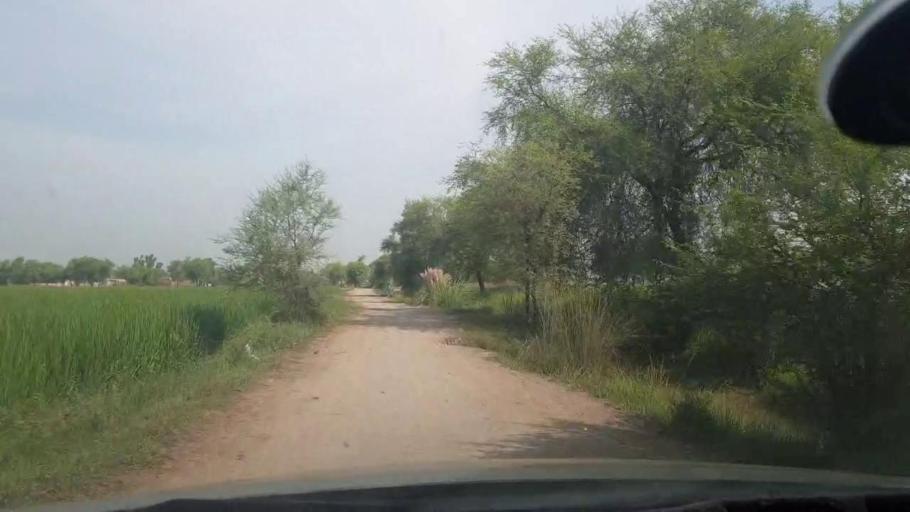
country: PK
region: Sindh
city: Jacobabad
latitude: 28.2943
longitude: 68.4803
